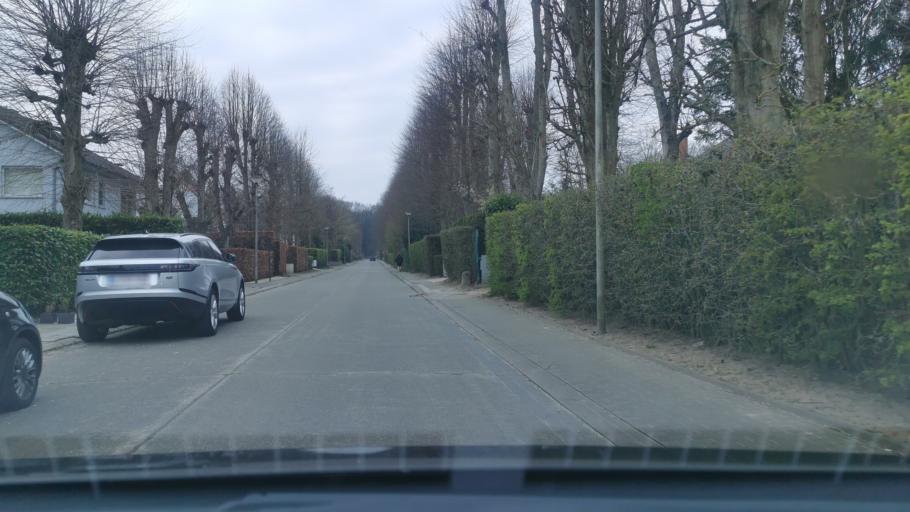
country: BE
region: Flanders
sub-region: Provincie Vlaams-Brabant
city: Tervuren
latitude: 50.8131
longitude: 4.4973
